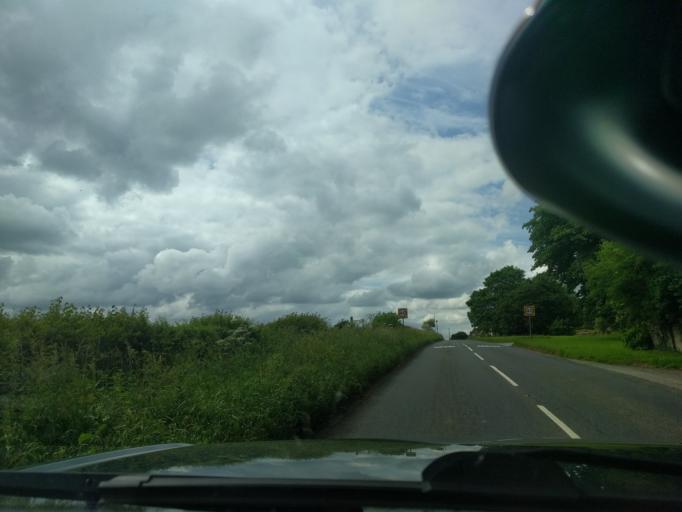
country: GB
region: England
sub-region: Wiltshire
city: Corsham
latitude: 51.4101
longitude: -2.1662
